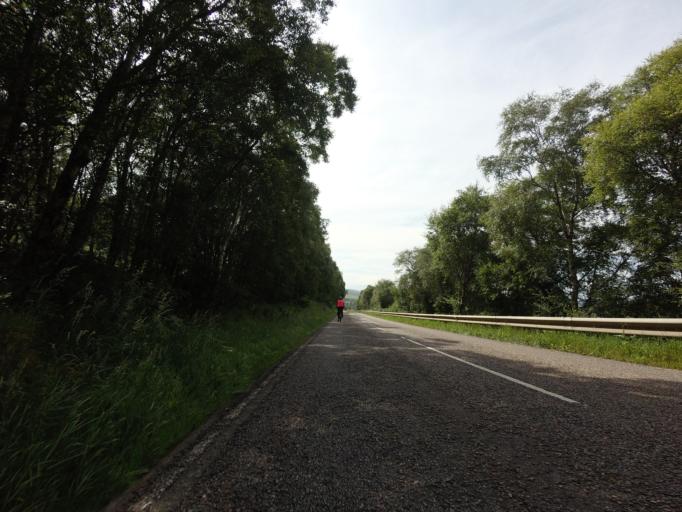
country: GB
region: Scotland
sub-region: Highland
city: Alness
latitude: 57.8546
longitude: -4.2564
